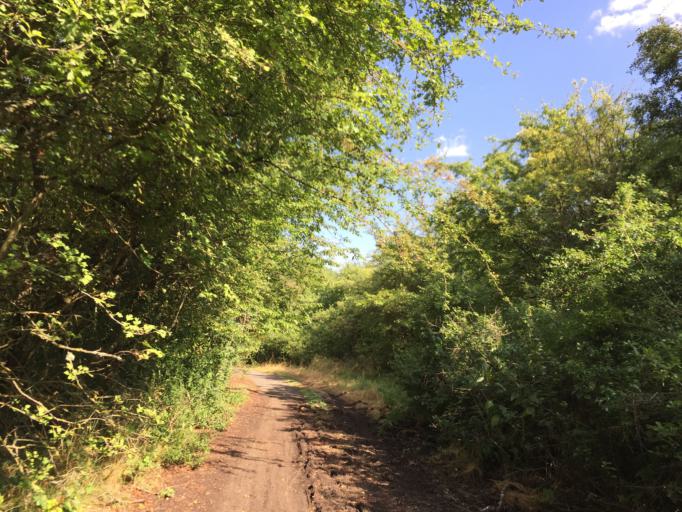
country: DE
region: Hesse
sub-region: Regierungsbezirk Giessen
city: Heuchelheim
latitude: 50.6028
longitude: 8.6317
